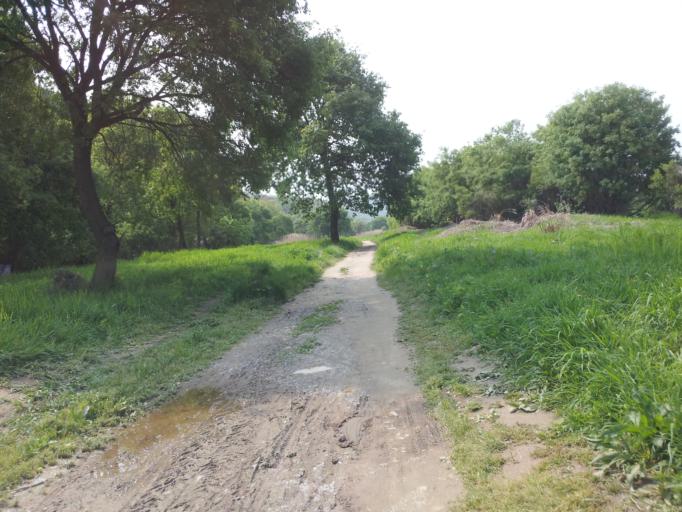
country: KR
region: Daejeon
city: Daejeon
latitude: 36.3398
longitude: 127.3535
